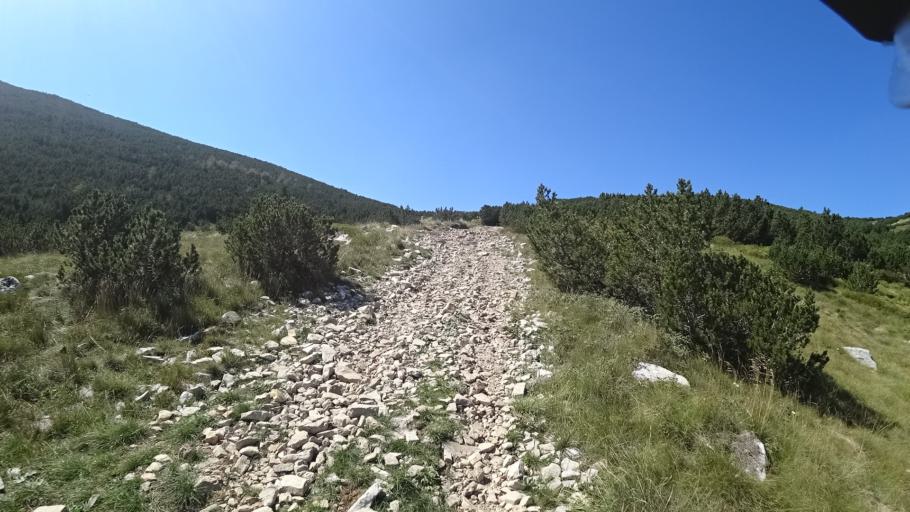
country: HR
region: Splitsko-Dalmatinska
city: Hrvace
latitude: 43.9387
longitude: 16.5777
